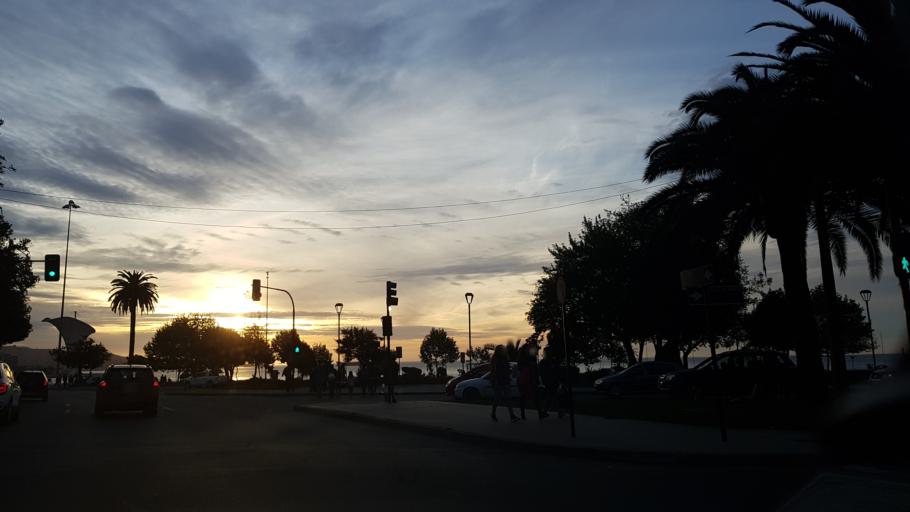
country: CL
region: Valparaiso
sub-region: Provincia de Valparaiso
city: Vina del Mar
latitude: -33.0237
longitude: -71.5677
